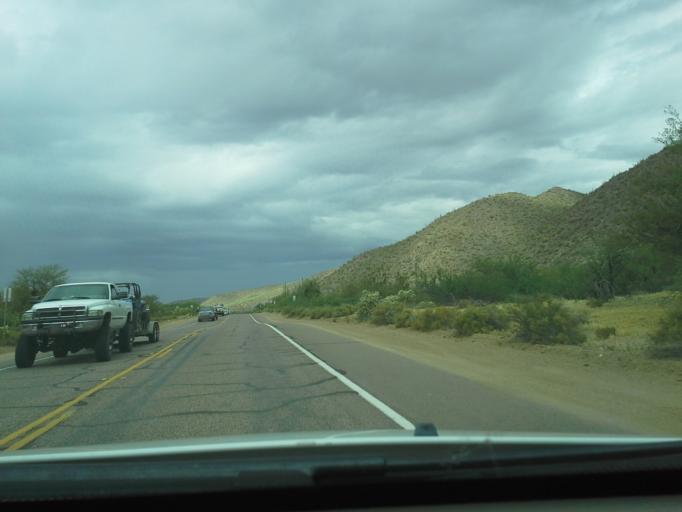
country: US
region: Arizona
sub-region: Pinal County
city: Apache Junction
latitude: 33.5521
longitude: -111.5624
